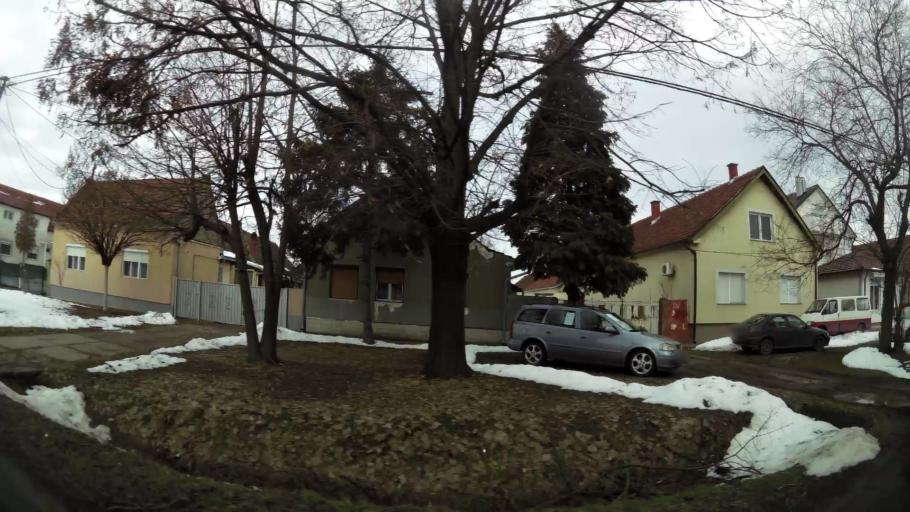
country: RS
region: Central Serbia
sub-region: Belgrade
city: Surcin
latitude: 44.7938
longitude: 20.2871
